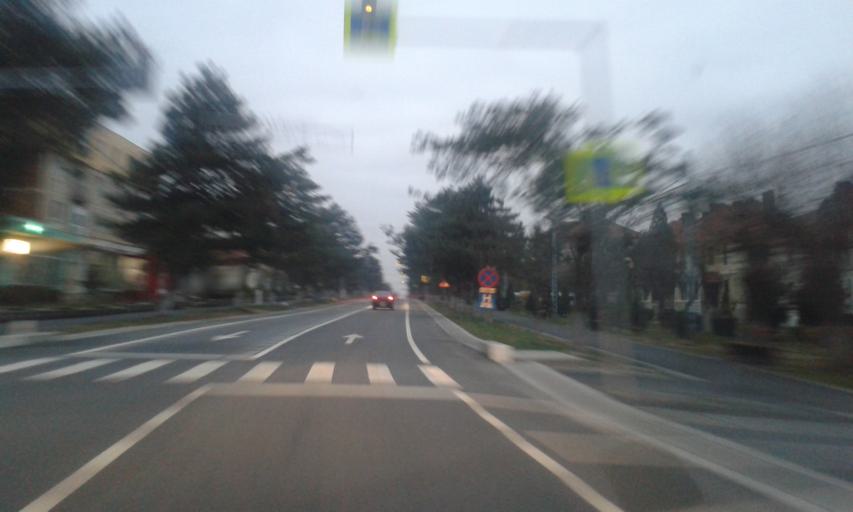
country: RO
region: Gorj
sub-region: Comuna Bumbesti-Jiu
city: Bumbesti-Jiu
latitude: 45.1809
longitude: 23.3794
